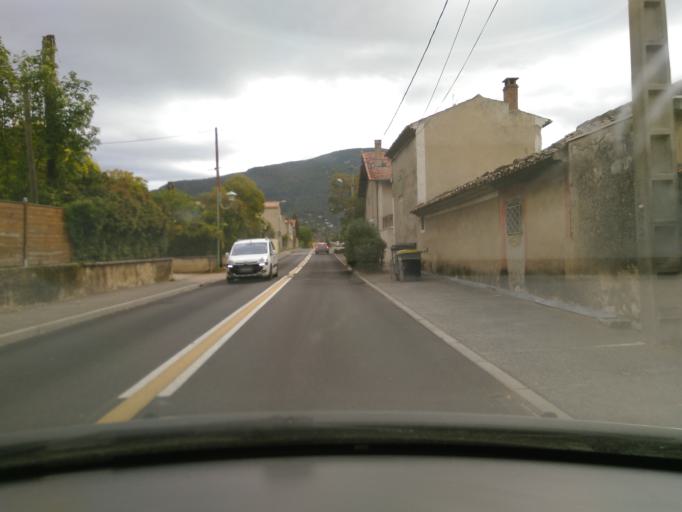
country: FR
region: Rhone-Alpes
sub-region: Departement de la Drome
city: Nyons
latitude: 44.3623
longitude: 5.1314
